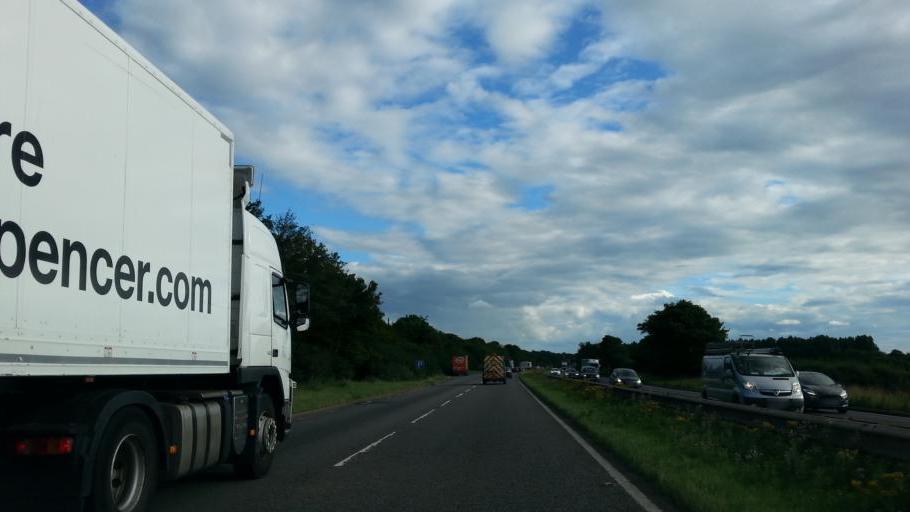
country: GB
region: England
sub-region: Nottinghamshire
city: Babworth
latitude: 53.3301
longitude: -1.0276
